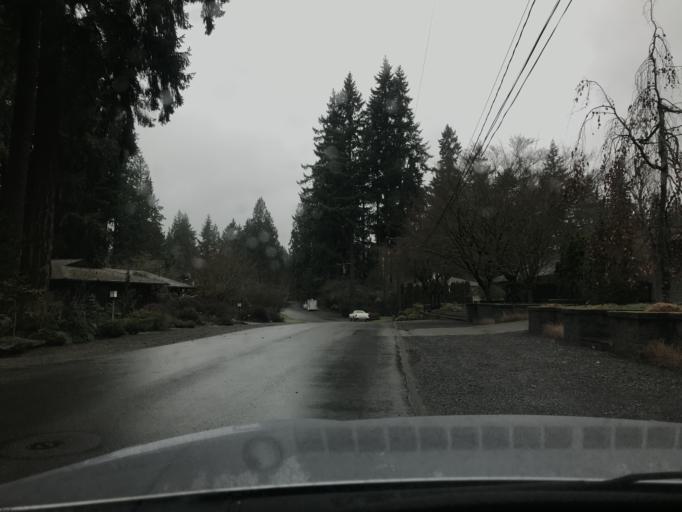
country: US
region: Washington
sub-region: King County
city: Bellevue
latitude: 47.6182
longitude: -122.1665
